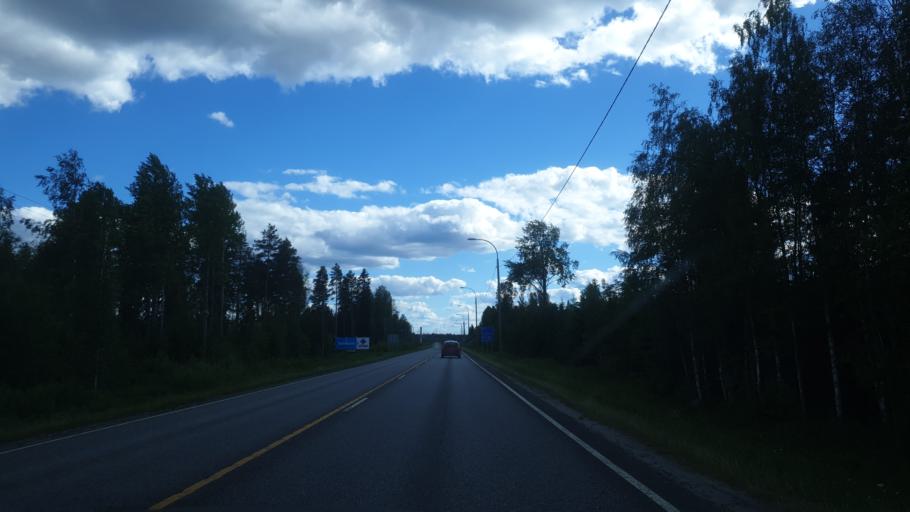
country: FI
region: Southern Savonia
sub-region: Pieksaemaeki
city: Juva
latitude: 61.9077
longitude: 27.8050
